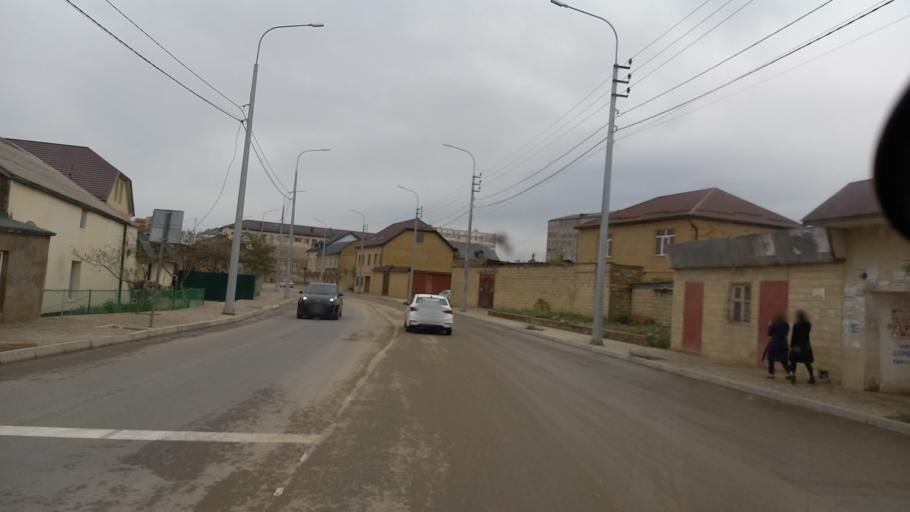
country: RU
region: Dagestan
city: Derbent
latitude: 42.0914
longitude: 48.2888
